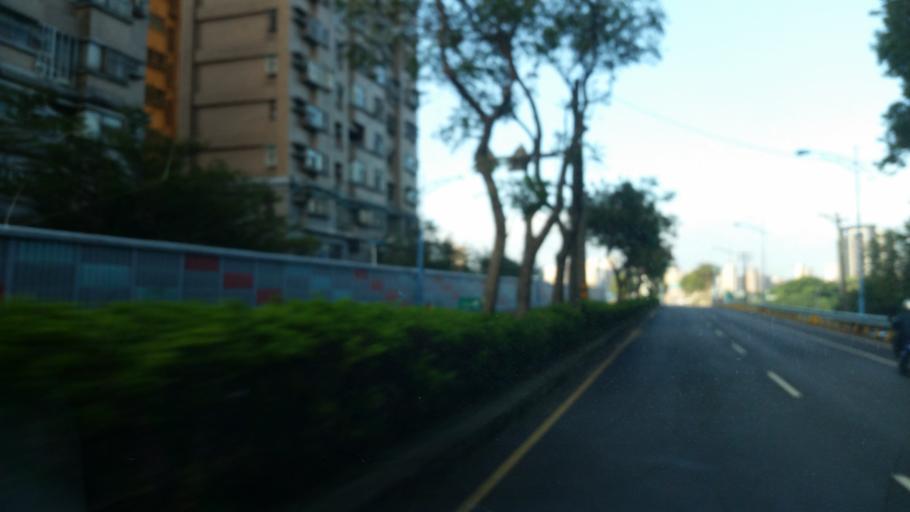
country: TW
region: Taiwan
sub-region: Taoyuan
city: Taoyuan
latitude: 24.9970
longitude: 121.3306
